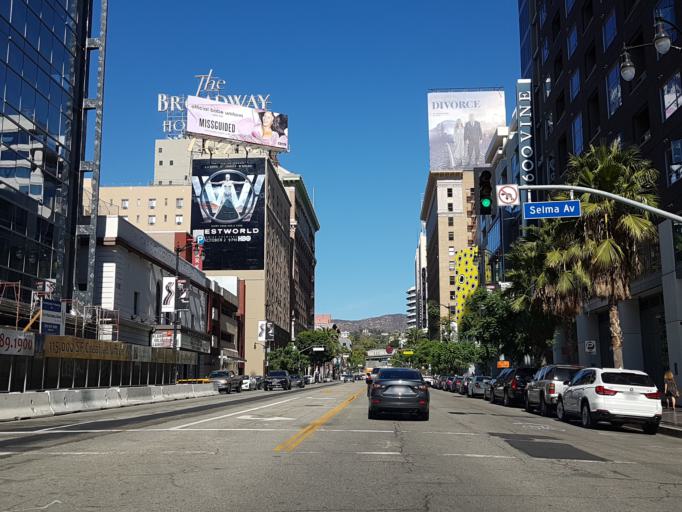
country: US
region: California
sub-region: Los Angeles County
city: Hollywood
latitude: 34.0997
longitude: -118.3267
